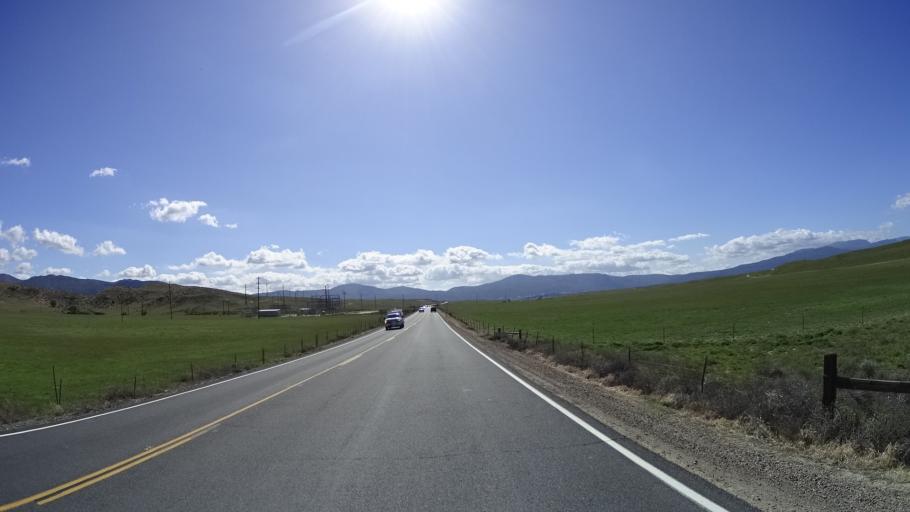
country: US
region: California
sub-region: San Diego County
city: Julian
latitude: 33.2493
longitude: -116.6742
